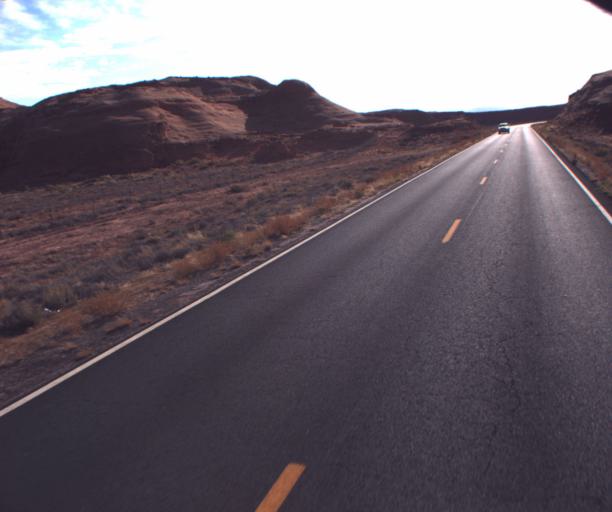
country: US
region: Arizona
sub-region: Apache County
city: Many Farms
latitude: 36.7679
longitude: -109.6565
